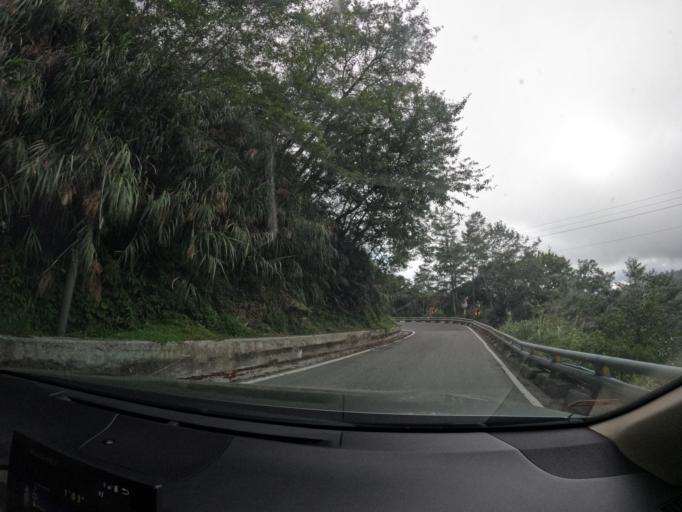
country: TW
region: Taiwan
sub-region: Taitung
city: Taitung
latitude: 23.2428
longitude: 120.9988
